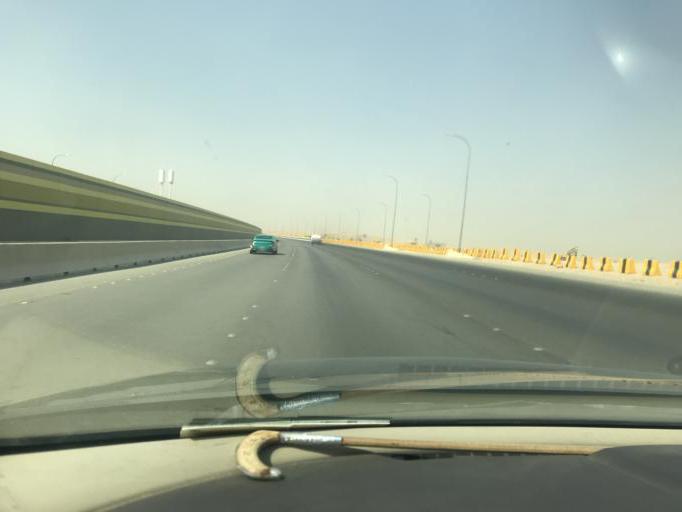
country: SA
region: Ar Riyad
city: Riyadh
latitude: 24.9008
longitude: 46.7025
